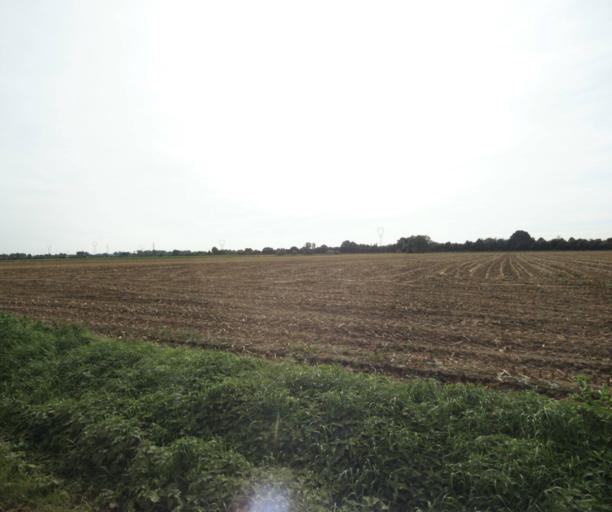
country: FR
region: Nord-Pas-de-Calais
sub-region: Departement du Nord
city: Ennetieres-en-Weppes
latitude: 50.6102
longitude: 2.9378
